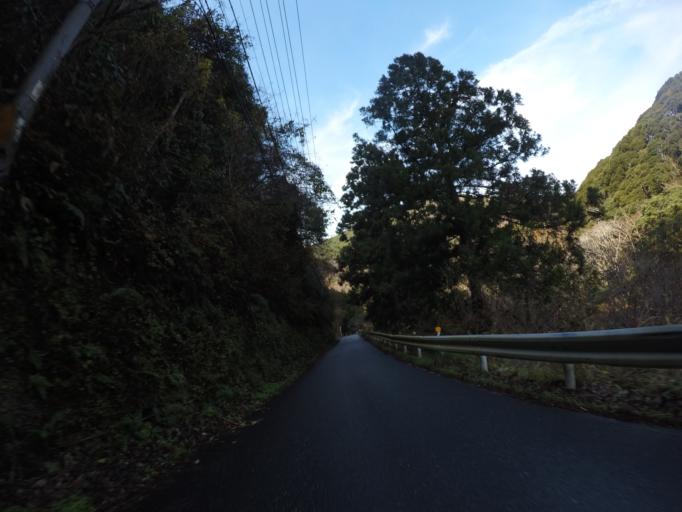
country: JP
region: Shizuoka
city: Heda
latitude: 34.8047
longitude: 138.8209
